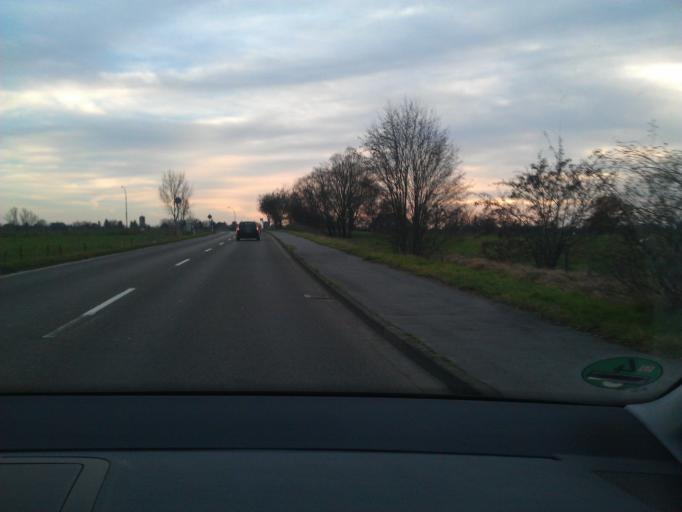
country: BE
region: Wallonia
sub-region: Province de Liege
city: Raeren
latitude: 50.7323
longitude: 6.1405
